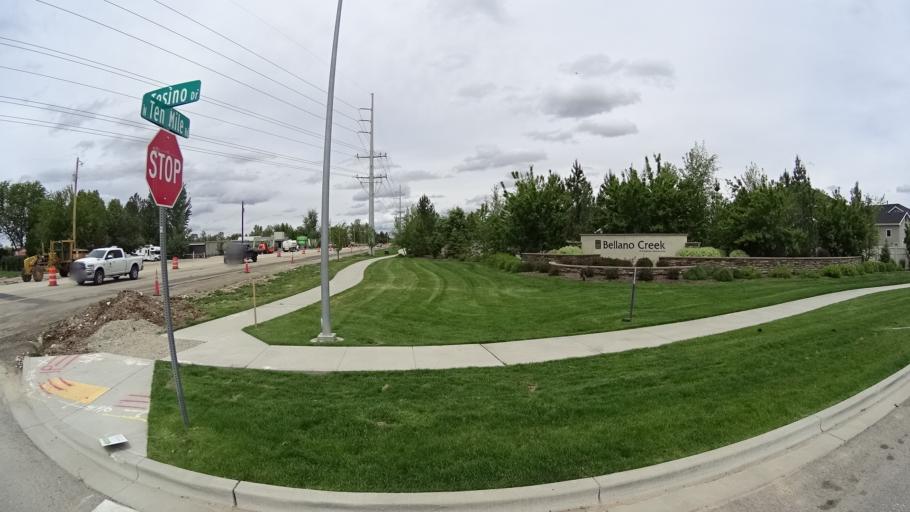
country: US
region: Idaho
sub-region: Ada County
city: Meridian
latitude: 43.6395
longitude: -116.4334
